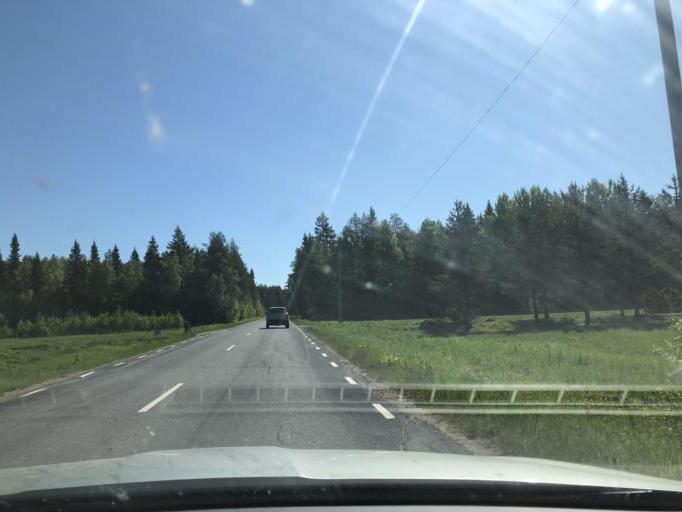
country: SE
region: Norrbotten
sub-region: Lulea Kommun
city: Gammelstad
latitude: 65.6564
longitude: 22.0041
